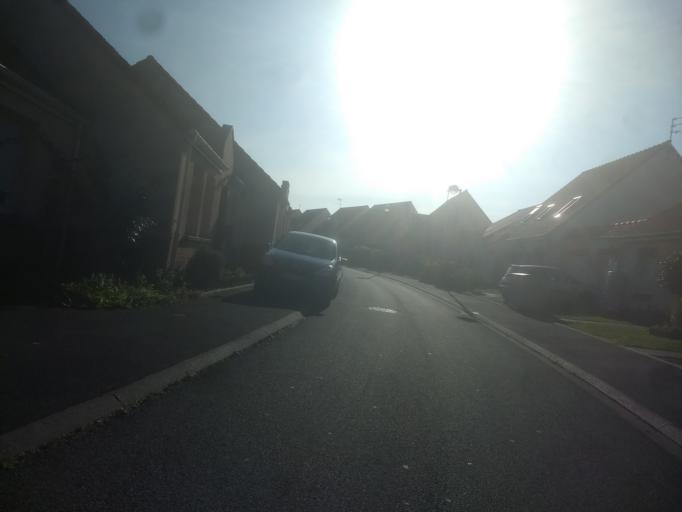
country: FR
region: Nord-Pas-de-Calais
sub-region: Departement du Pas-de-Calais
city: Achicourt
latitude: 50.2732
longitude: 2.7765
